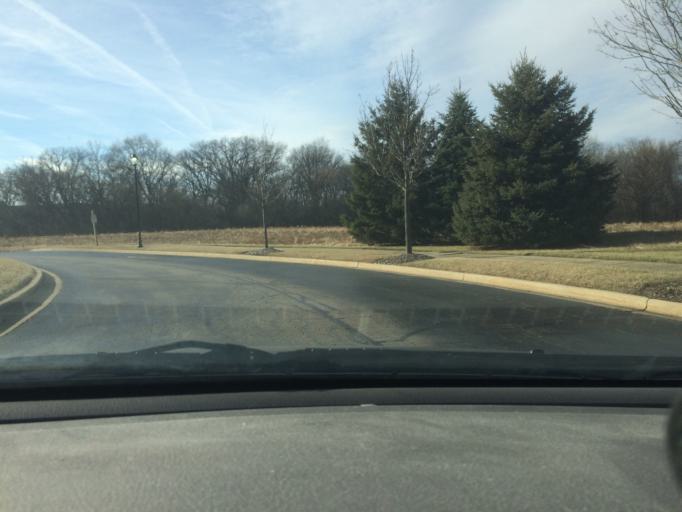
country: US
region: Illinois
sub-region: Kane County
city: Sleepy Hollow
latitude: 42.0777
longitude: -88.2899
